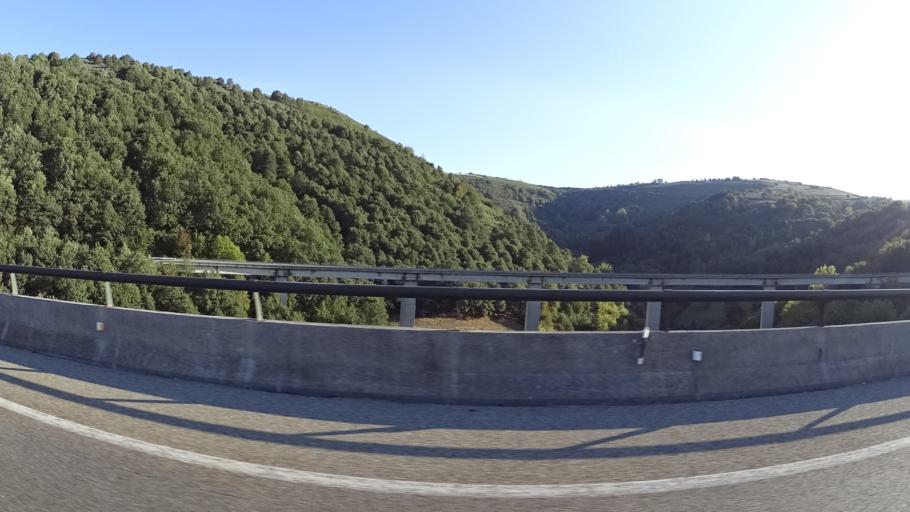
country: ES
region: Galicia
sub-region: Provincia de Lugo
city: San Roman
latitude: 42.7489
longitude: -7.0581
